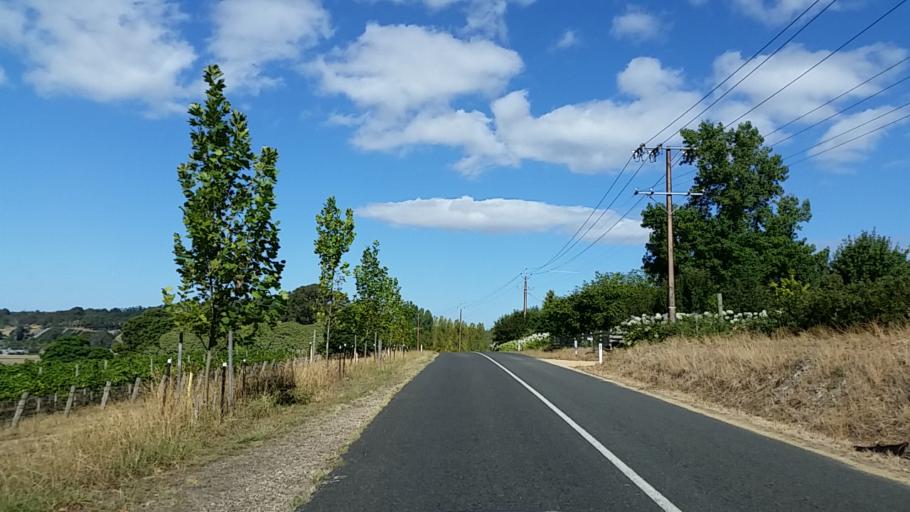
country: AU
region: South Australia
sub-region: Adelaide Hills
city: Bridgewater
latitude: -34.9677
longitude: 138.7272
